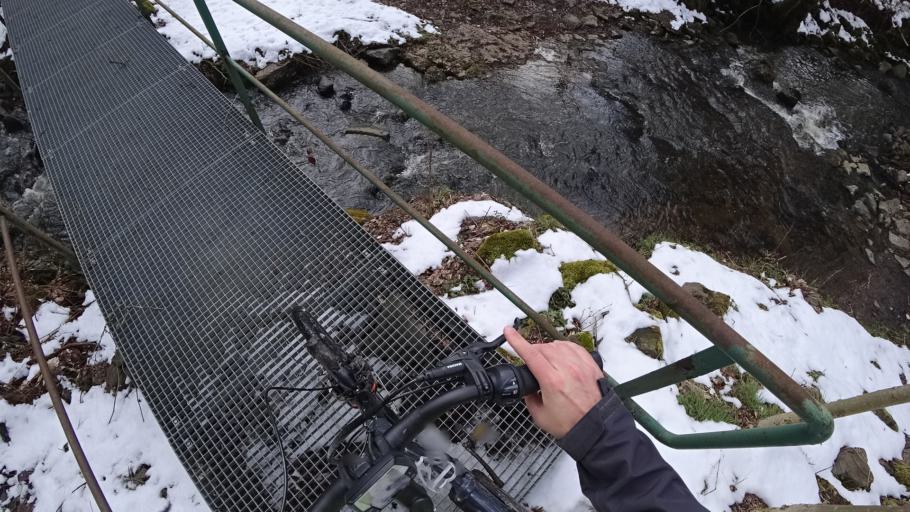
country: DE
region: Rheinland-Pfalz
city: Elkenroth
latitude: 50.7325
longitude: 7.8785
